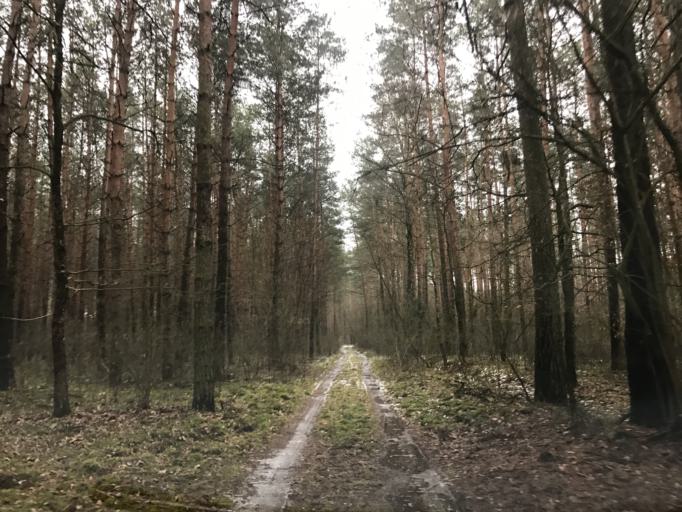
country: PL
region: Kujawsko-Pomorskie
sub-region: Powiat brodnicki
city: Bartniczka
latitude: 53.2866
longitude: 19.5703
